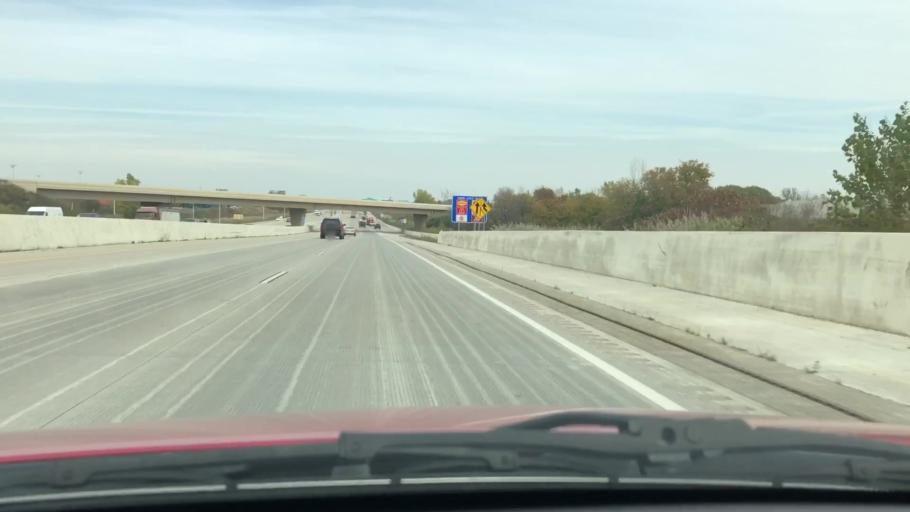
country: US
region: Wisconsin
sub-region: Brown County
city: De Pere
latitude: 44.4545
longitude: -88.0884
